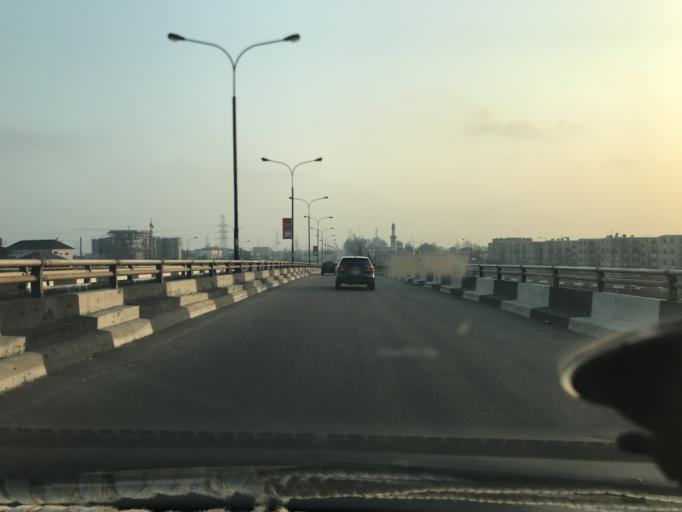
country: NG
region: Lagos
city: Lagos
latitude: 6.4563
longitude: 3.4083
